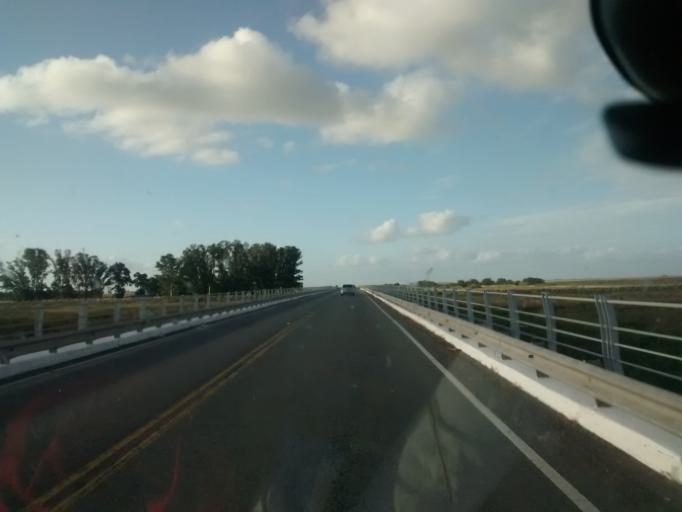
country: AR
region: Buenos Aires
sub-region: Partido de General Belgrano
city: General Belgrano
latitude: -36.1376
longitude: -58.5942
